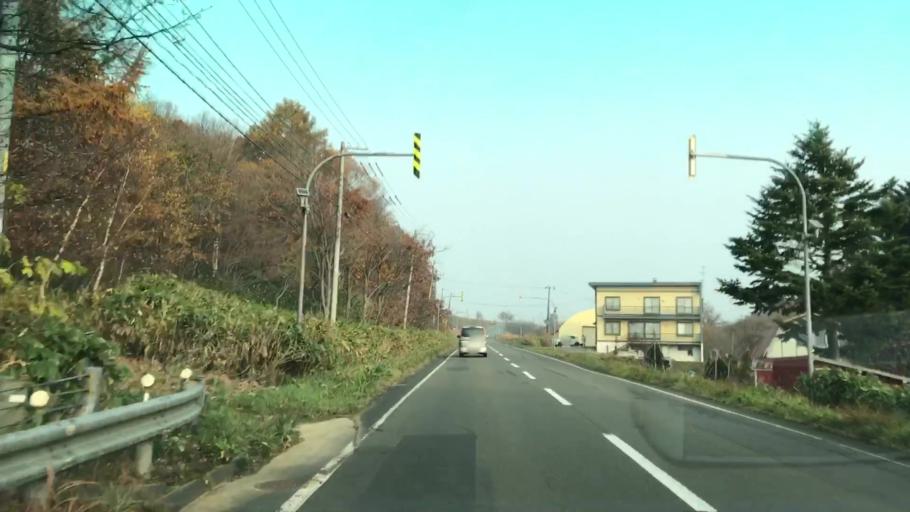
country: JP
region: Hokkaido
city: Ishikari
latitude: 43.3279
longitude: 141.4422
